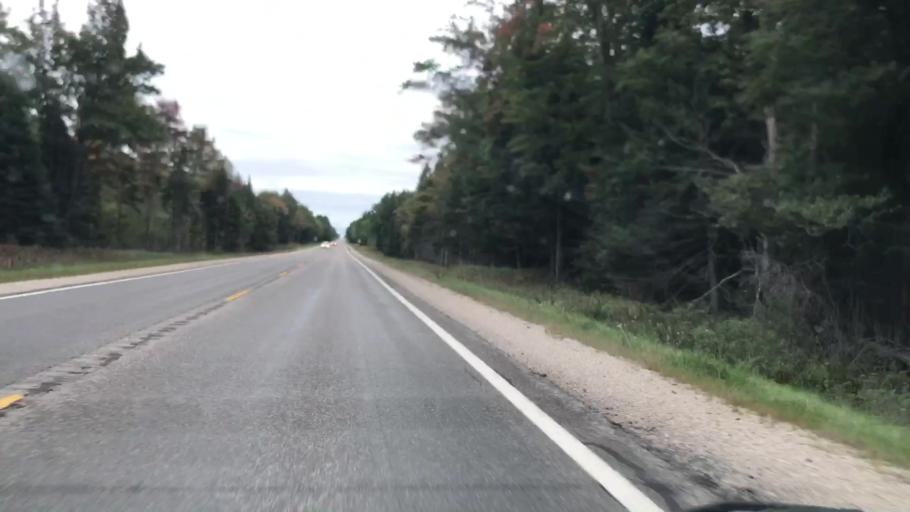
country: US
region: Michigan
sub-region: Luce County
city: Newberry
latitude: 46.2346
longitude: -85.5722
